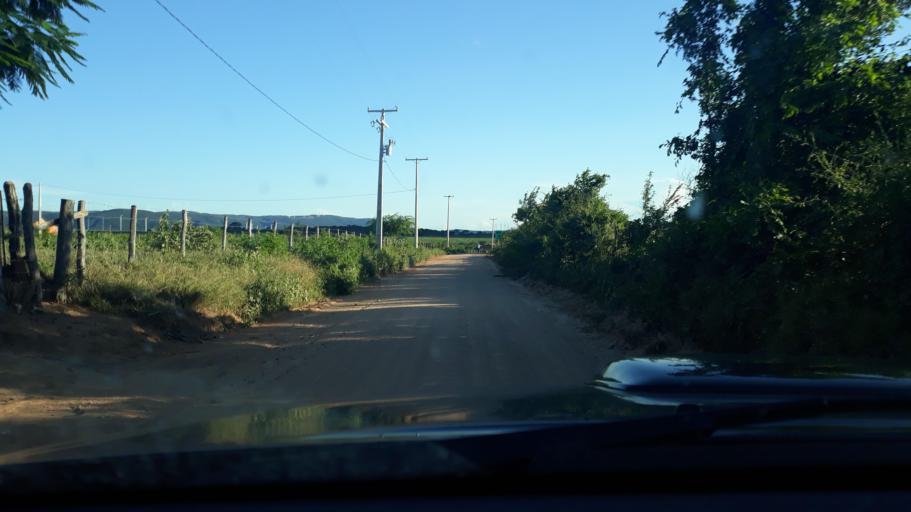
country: BR
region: Bahia
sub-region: Riacho De Santana
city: Riacho de Santana
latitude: -13.7933
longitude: -42.7119
